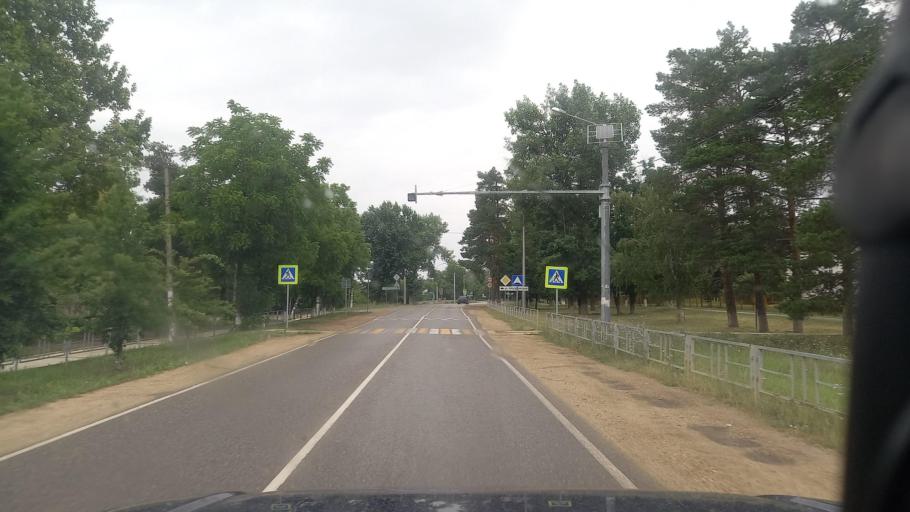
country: RU
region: Krasnodarskiy
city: Ryazanskaya
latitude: 44.9544
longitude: 39.5888
